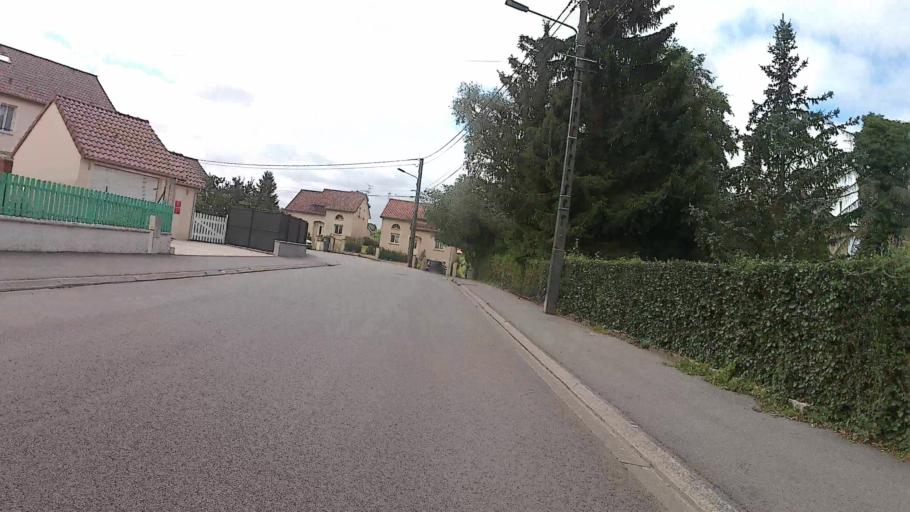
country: FR
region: Lorraine
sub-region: Departement de la Meuse
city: Verdun
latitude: 49.1609
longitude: 5.3954
